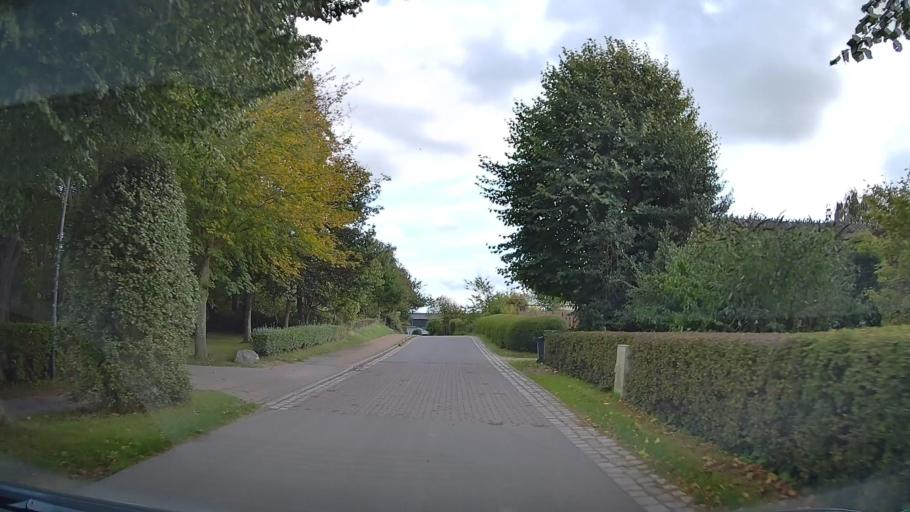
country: DE
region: Schleswig-Holstein
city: Steinberg
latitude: 54.7720
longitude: 9.8047
